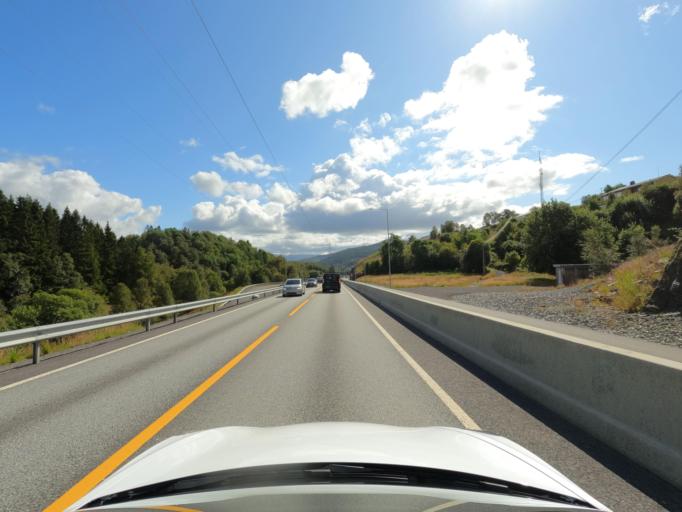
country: NO
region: Hordaland
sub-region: Bergen
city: Hylkje
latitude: 60.4772
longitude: 5.3167
